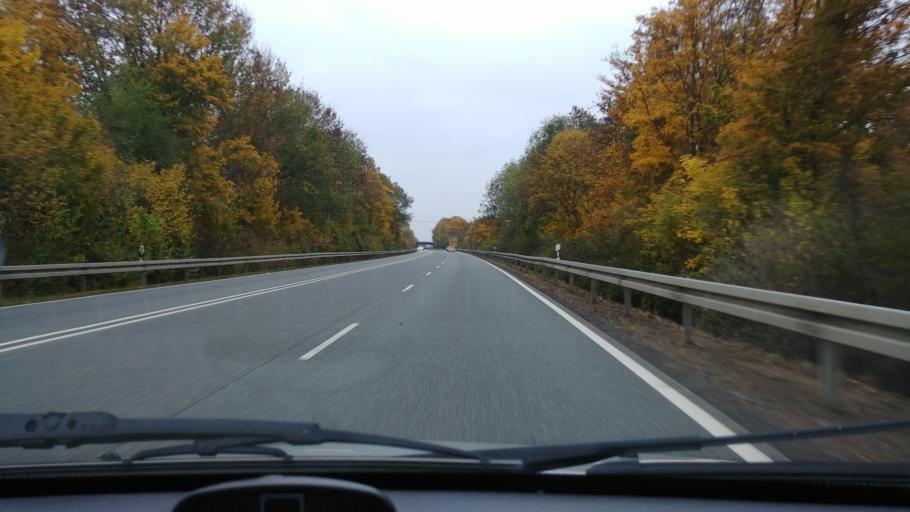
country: DE
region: Hesse
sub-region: Regierungsbezirk Giessen
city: Dehrn
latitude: 50.4494
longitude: 8.0882
